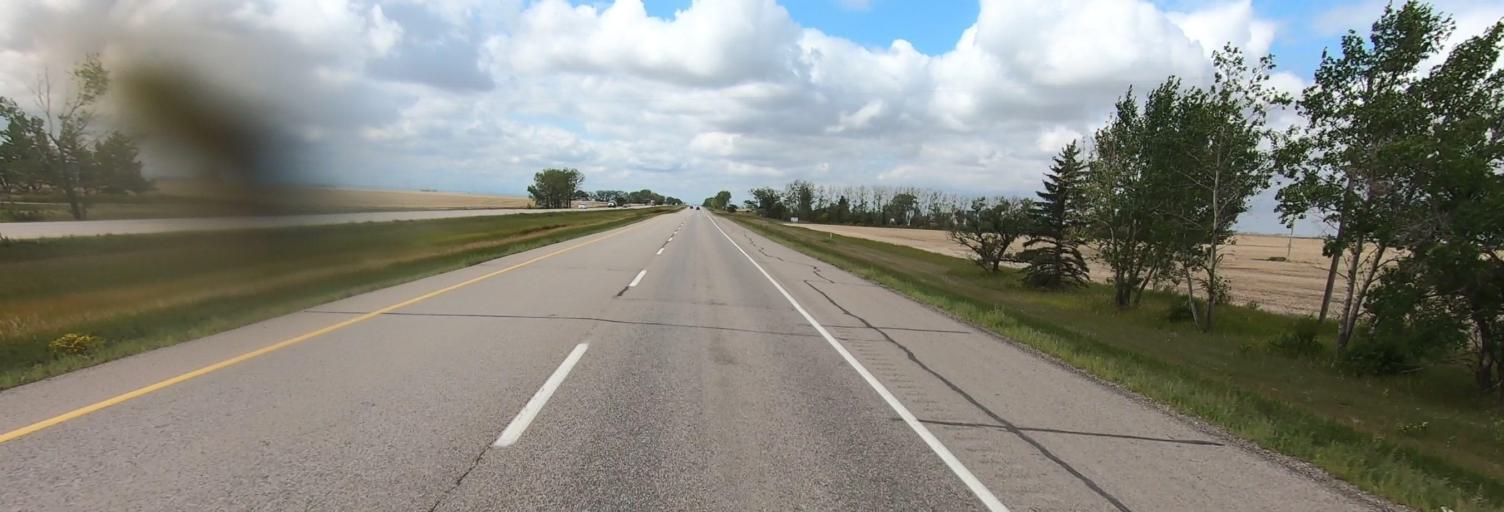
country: CA
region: Saskatchewan
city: Moose Jaw
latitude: 50.3974
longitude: -105.3101
